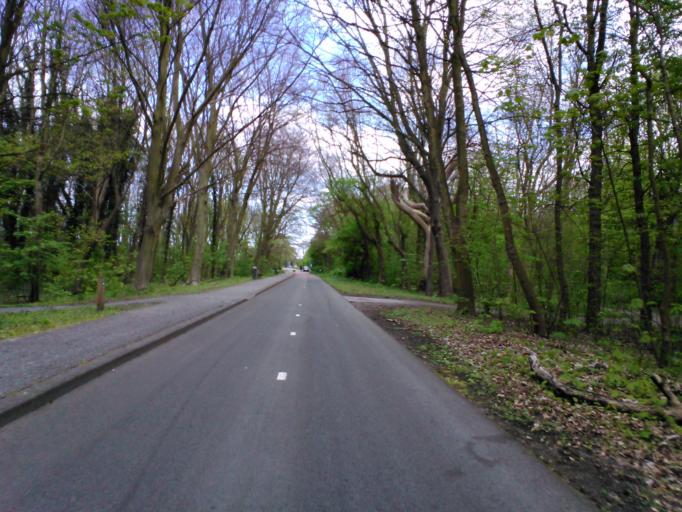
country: NL
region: South Holland
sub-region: Gemeente Rotterdam
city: Hoek van Holland
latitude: 51.9860
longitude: 4.1226
